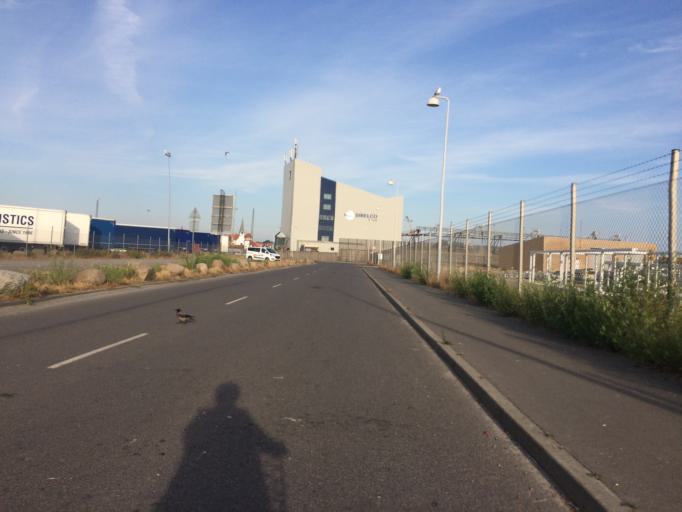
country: DK
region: Capital Region
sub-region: Bornholm Kommune
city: Ronne
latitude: 55.1010
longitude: 14.6852
